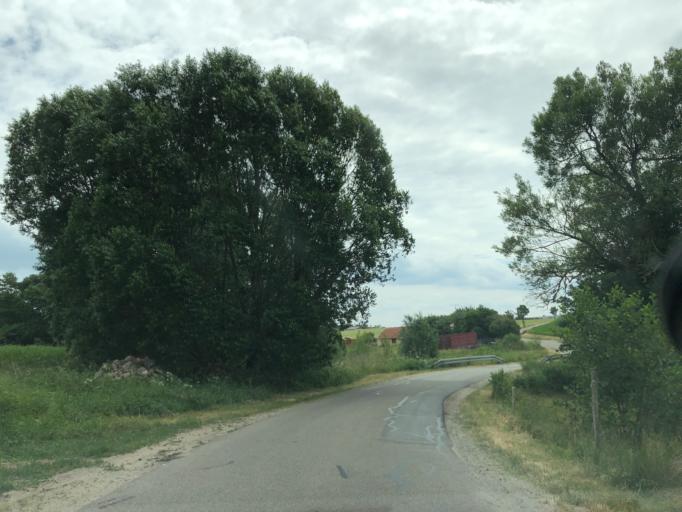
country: DK
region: Central Jutland
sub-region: Silkeborg Kommune
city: Svejbaek
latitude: 56.2007
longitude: 9.6902
